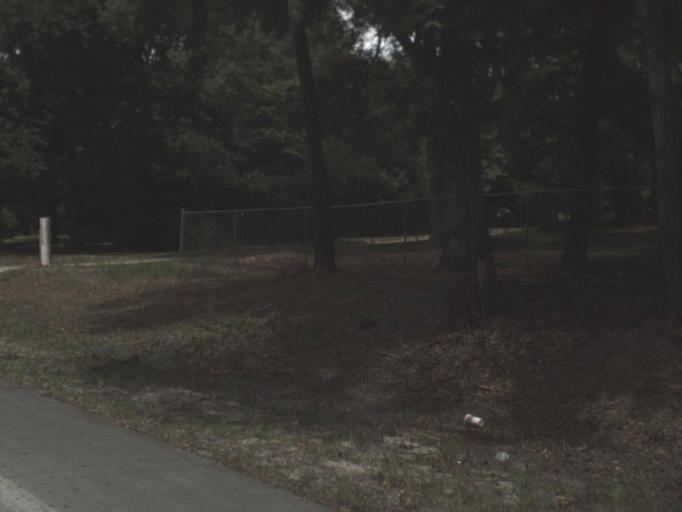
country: US
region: Florida
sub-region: Alachua County
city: High Springs
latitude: 29.8052
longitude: -82.6081
